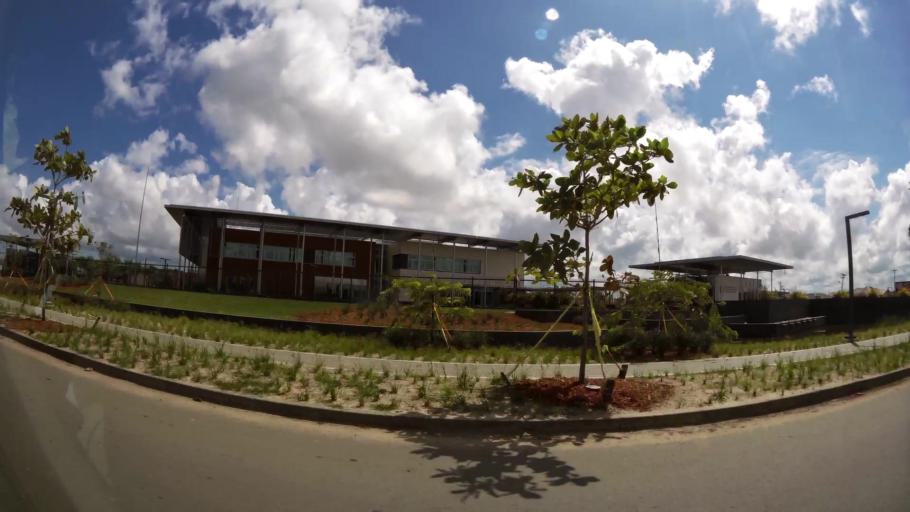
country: SR
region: Paramaribo
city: Paramaribo
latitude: 5.8634
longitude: -55.1272
